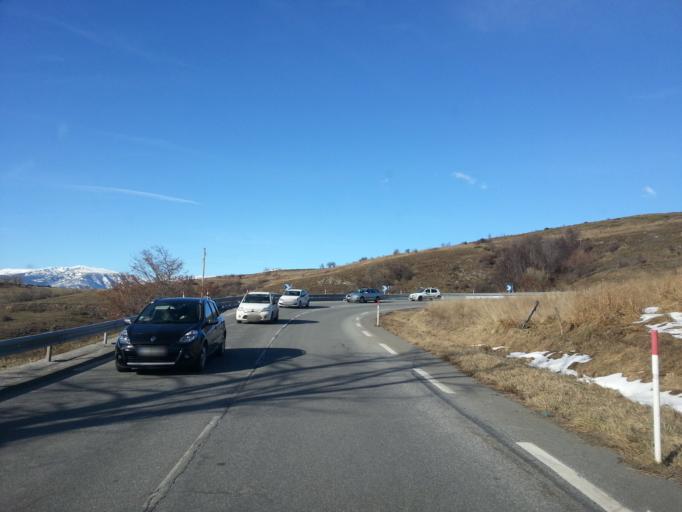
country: ES
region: Catalonia
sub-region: Provincia de Girona
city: Llivia
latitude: 42.4695
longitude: 2.0349
